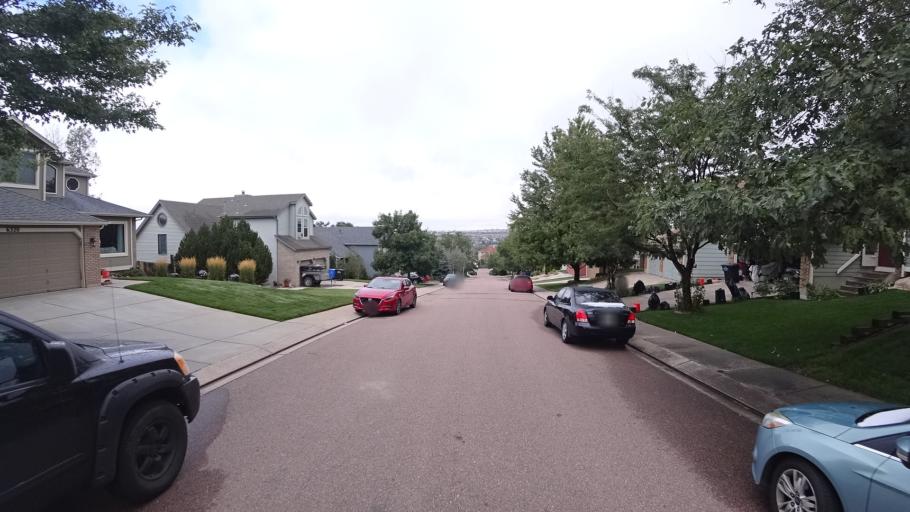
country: US
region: Colorado
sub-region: El Paso County
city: Cimarron Hills
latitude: 38.9226
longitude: -104.7588
